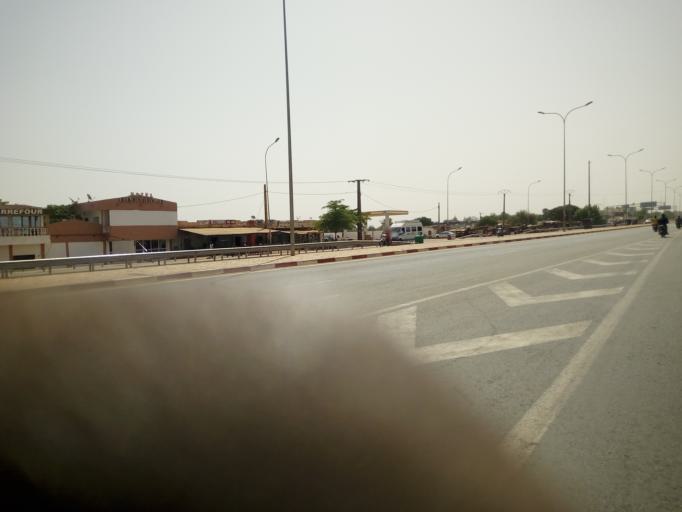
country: ML
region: Segou
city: Segou
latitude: 13.4370
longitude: -6.2372
